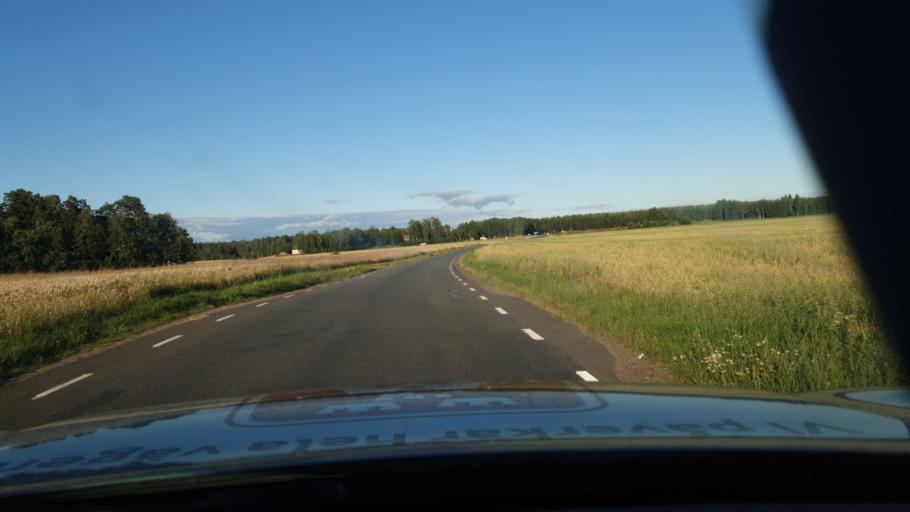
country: SE
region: Vaestra Goetaland
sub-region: Skovde Kommun
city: Stopen
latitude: 58.4754
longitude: 13.9455
